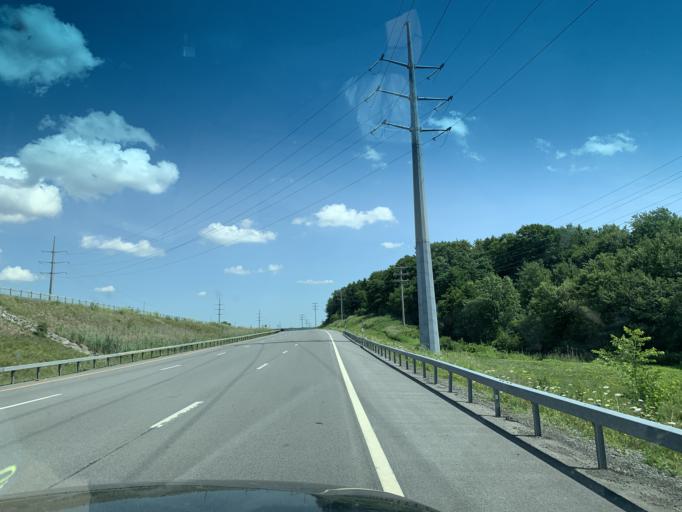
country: US
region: New York
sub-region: Oneida County
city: New York Mills
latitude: 43.0909
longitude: -75.3084
